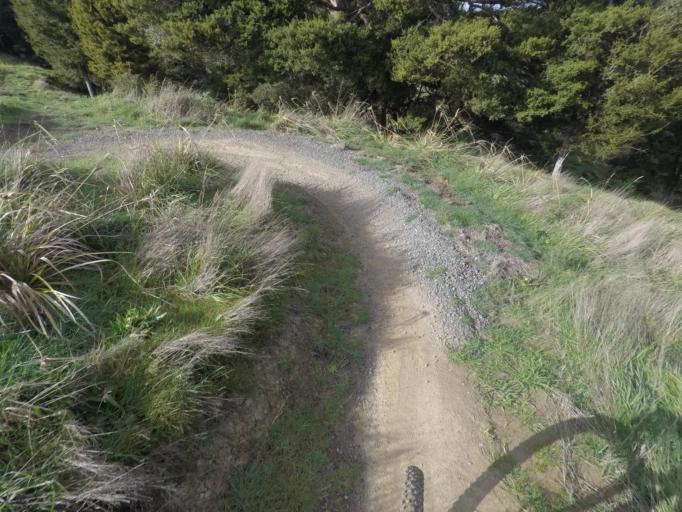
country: NZ
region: Auckland
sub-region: Auckland
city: Manukau City
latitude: -36.9963
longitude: 174.9112
